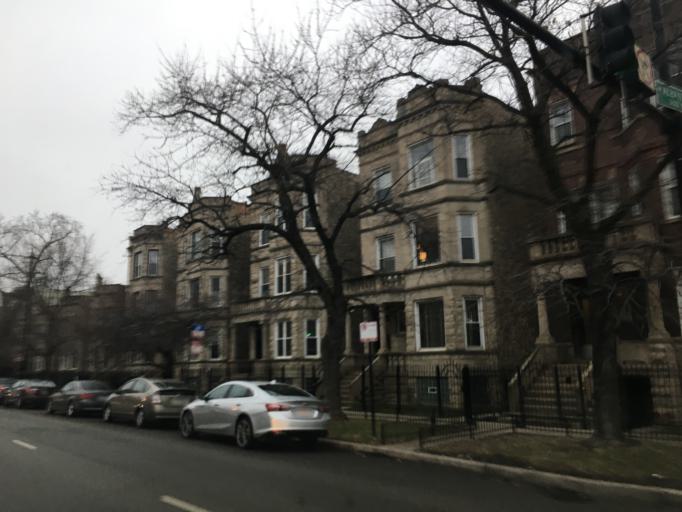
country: US
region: Illinois
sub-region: Cook County
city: Lincolnwood
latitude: 41.9247
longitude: -87.7047
